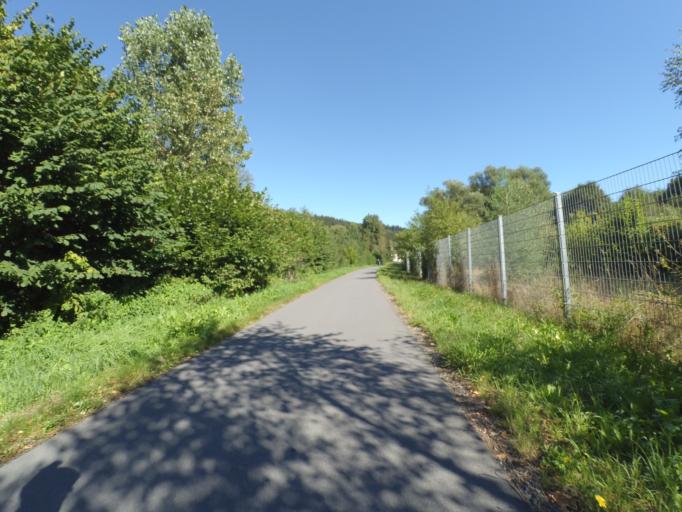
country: DE
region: Rheinland-Pfalz
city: Daun
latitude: 50.2019
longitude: 6.8330
